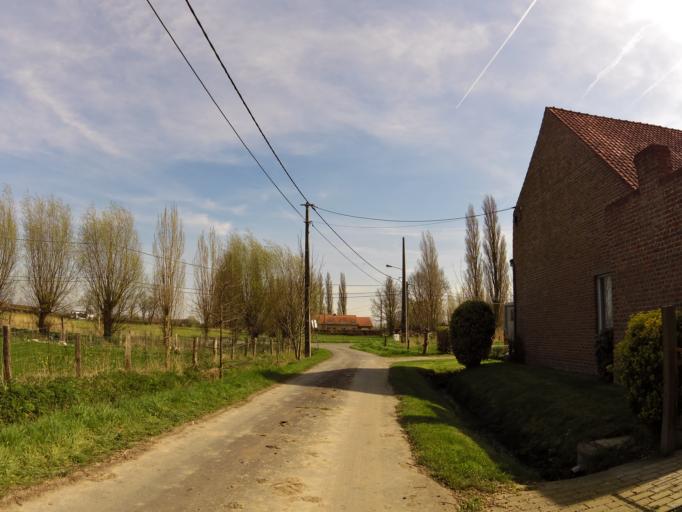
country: BE
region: Flanders
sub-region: Provincie West-Vlaanderen
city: Oudenburg
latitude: 51.1860
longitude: 3.0272
